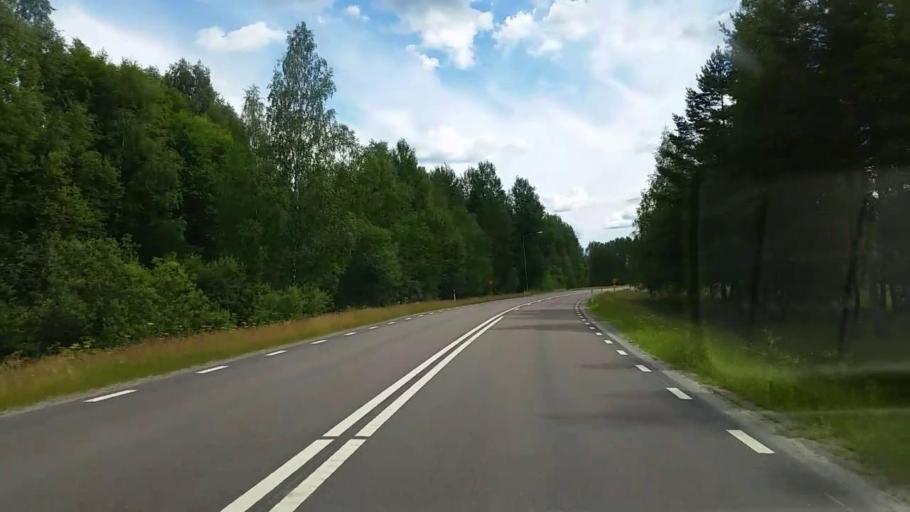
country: SE
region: Gaevleborg
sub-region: Ovanakers Kommun
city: Edsbyn
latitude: 61.3816
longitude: 15.8328
